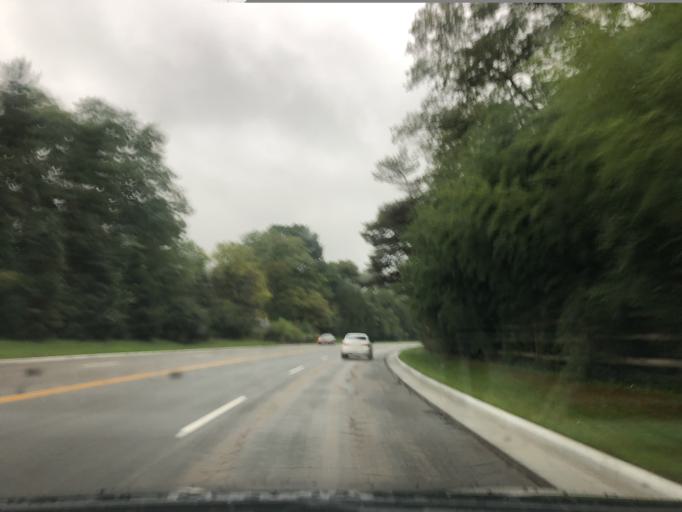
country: US
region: Ohio
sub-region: Hamilton County
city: Blue Ash
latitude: 39.2354
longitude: -84.3917
